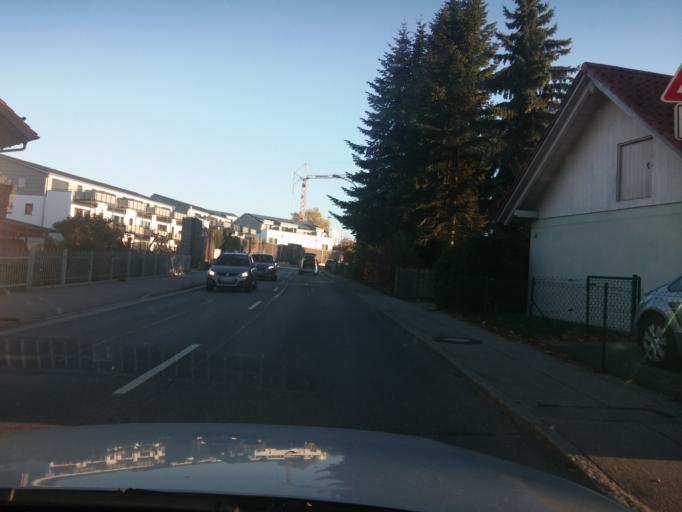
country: DE
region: Bavaria
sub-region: Upper Bavaria
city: Dorfen
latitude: 48.2720
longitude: 12.1543
